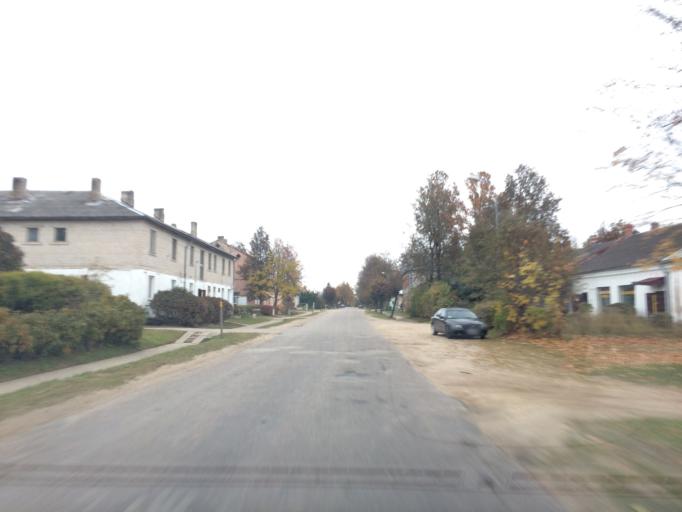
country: LV
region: Plavinu
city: Plavinas
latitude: 56.6133
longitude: 25.7720
